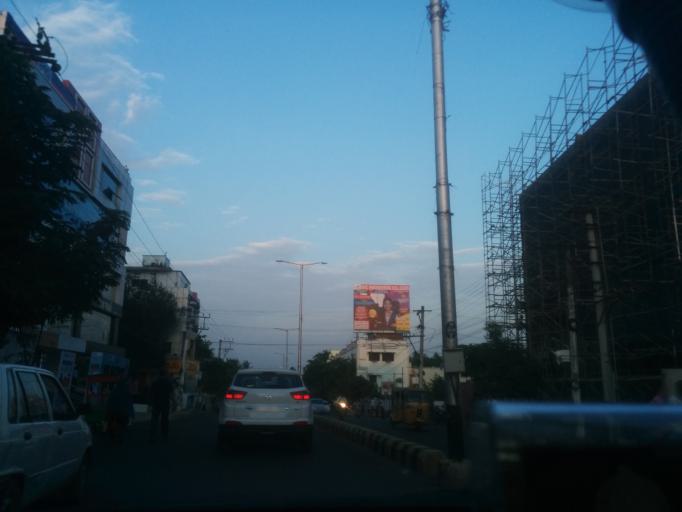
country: IN
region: Andhra Pradesh
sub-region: East Godavari
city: Rajahmundry
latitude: 17.0078
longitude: 81.7926
